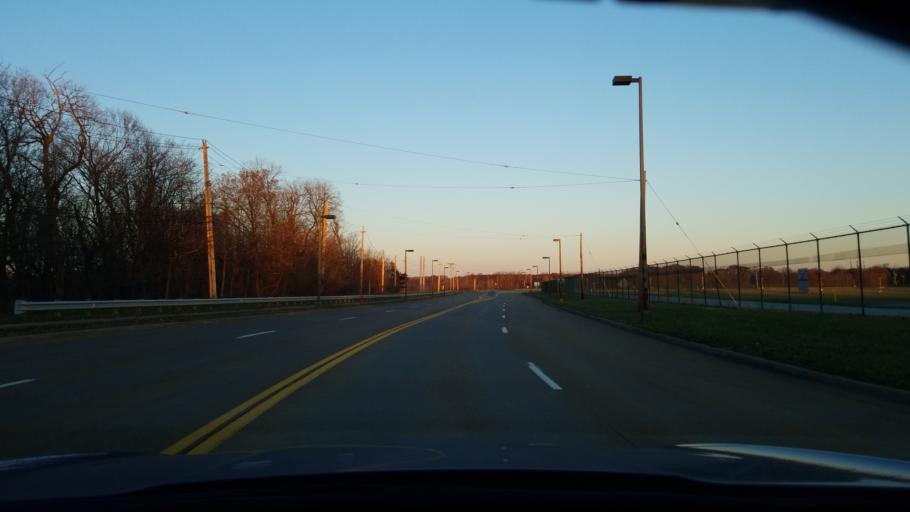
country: US
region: Ohio
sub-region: Cuyahoga County
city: Berea
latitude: 41.3930
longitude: -81.8770
